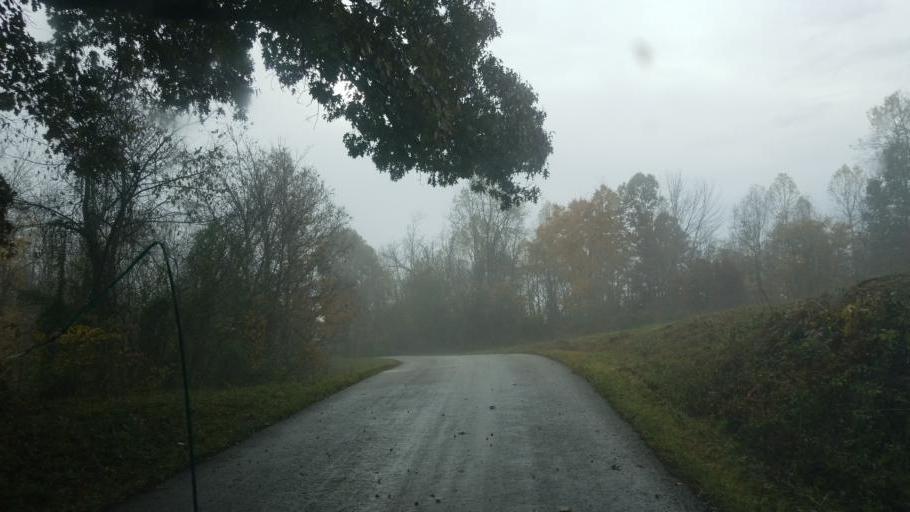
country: US
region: Ohio
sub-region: Morgan County
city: McConnelsville
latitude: 39.4964
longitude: -81.8157
